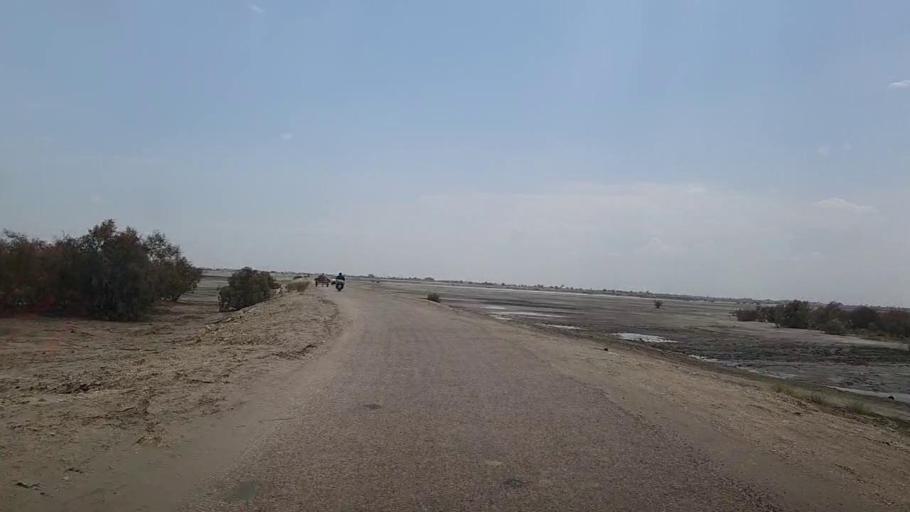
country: PK
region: Sindh
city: Kandhkot
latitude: 28.2872
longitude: 69.1515
